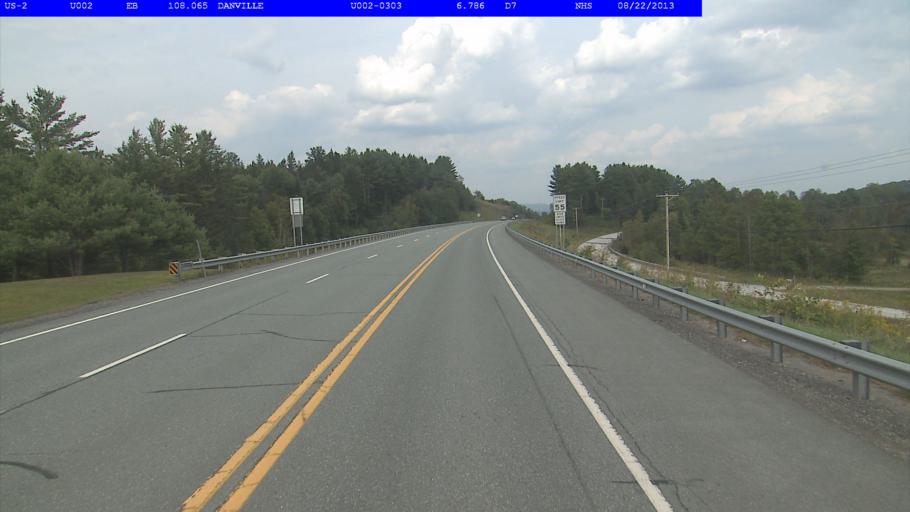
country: US
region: Vermont
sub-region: Caledonia County
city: St Johnsbury
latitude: 44.4303
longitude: -72.1017
